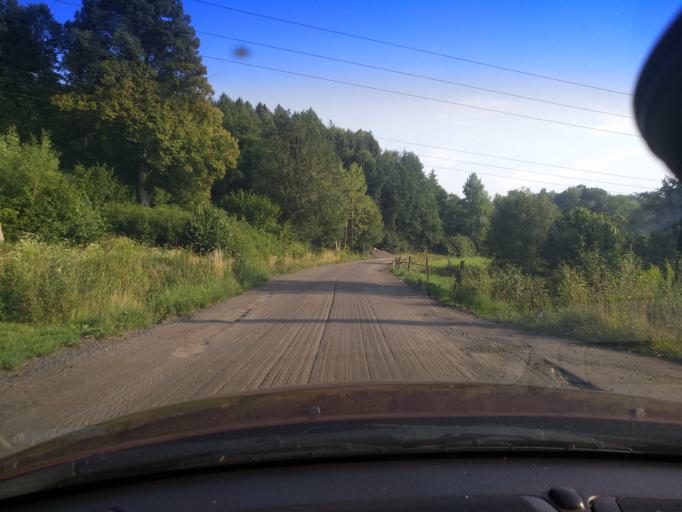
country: PL
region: Lower Silesian Voivodeship
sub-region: Powiat lubanski
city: Lesna
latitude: 51.0191
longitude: 15.2752
